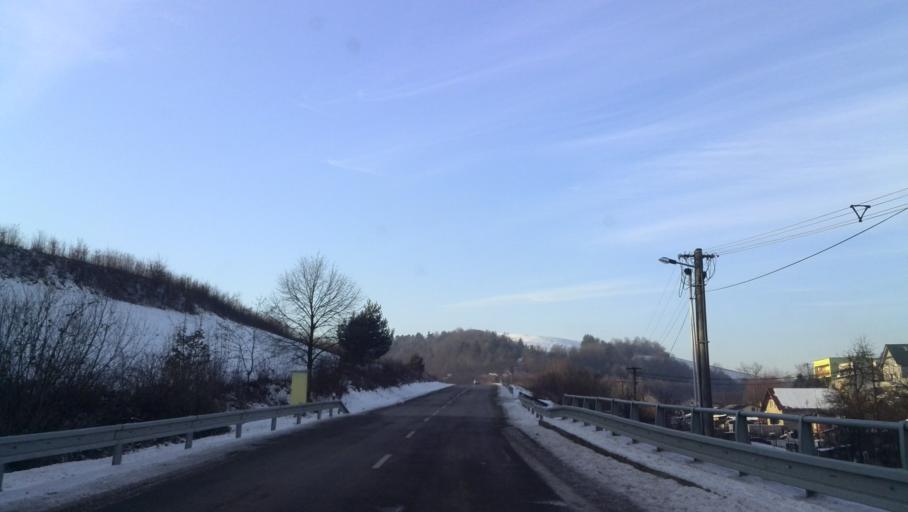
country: SK
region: Presovsky
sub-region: Okres Presov
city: Presov
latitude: 48.9626
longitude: 21.1353
